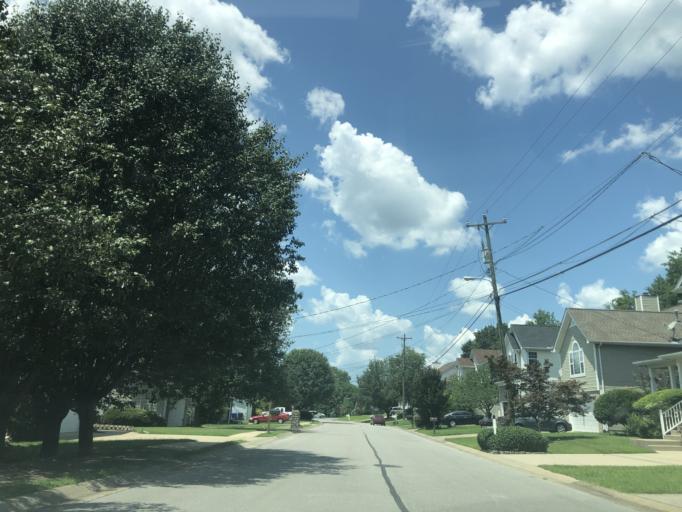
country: US
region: Tennessee
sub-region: Wilson County
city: Green Hill
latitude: 36.1638
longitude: -86.5830
